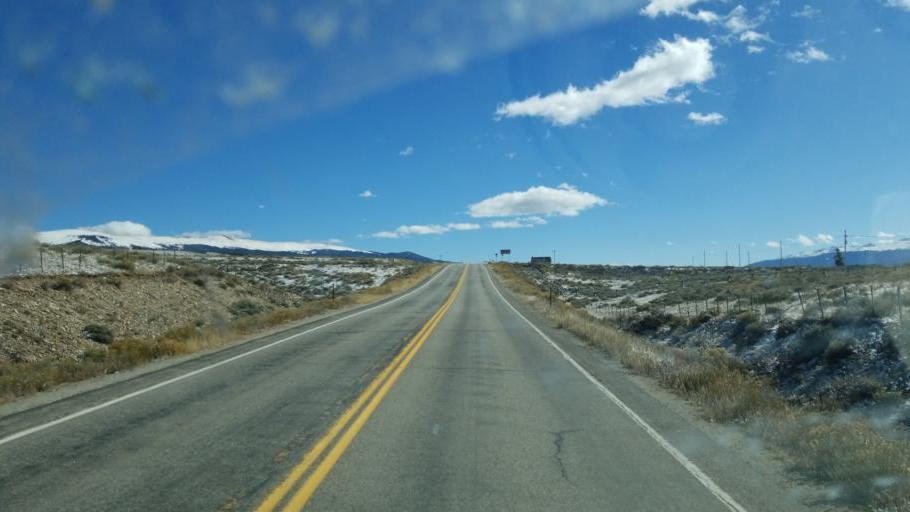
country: US
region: Colorado
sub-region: Lake County
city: Leadville
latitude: 39.1953
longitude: -106.3367
